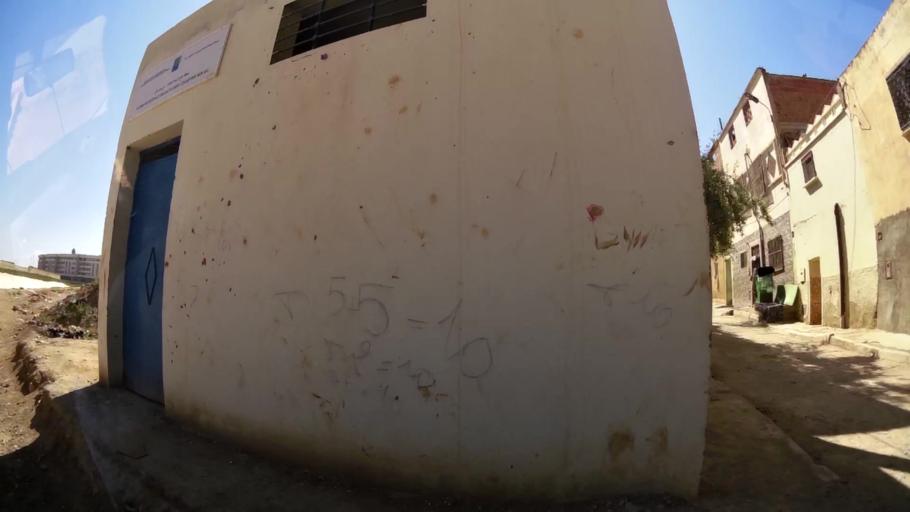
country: MA
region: Oriental
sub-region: Oujda-Angad
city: Oujda
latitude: 34.6805
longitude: -1.9258
